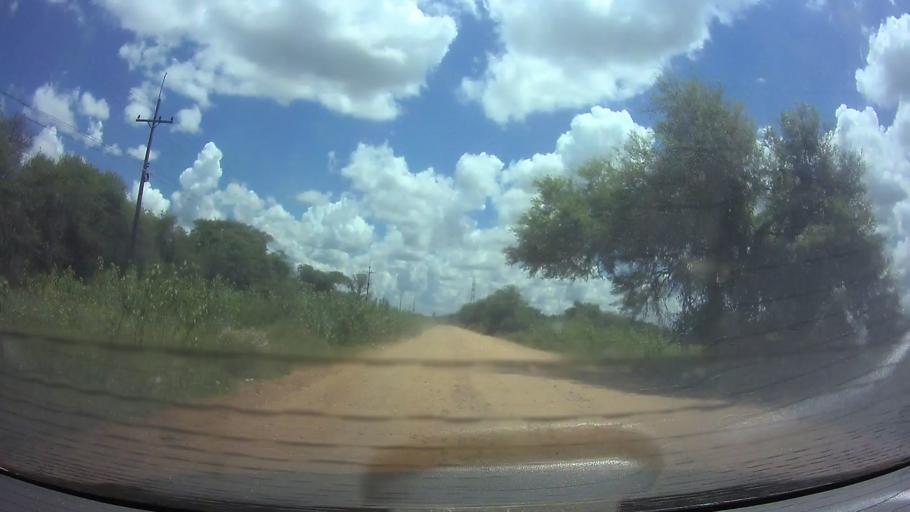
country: PY
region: Presidente Hayes
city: Nanawa
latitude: -25.2454
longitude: -57.6597
